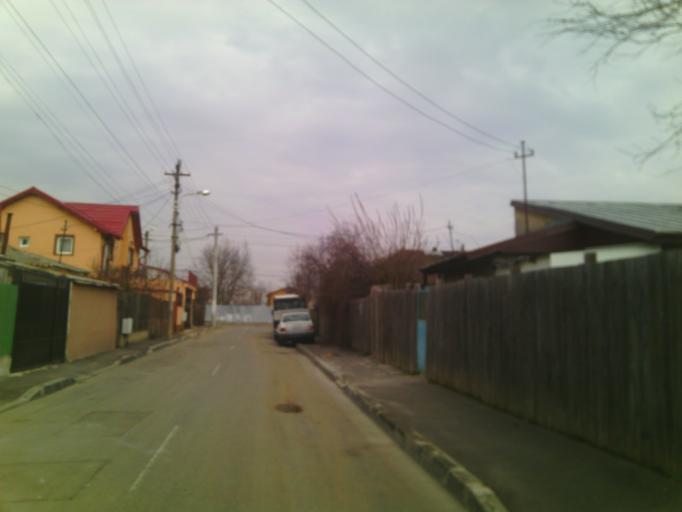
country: RO
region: Ilfov
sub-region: Comuna Jilava
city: Jilava
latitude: 44.3713
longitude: 26.0997
